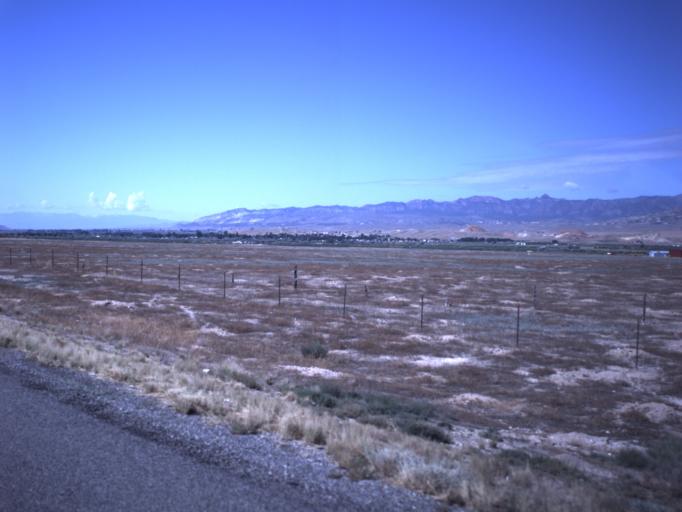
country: US
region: Utah
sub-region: Sevier County
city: Salina
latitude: 39.0292
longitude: -111.8302
